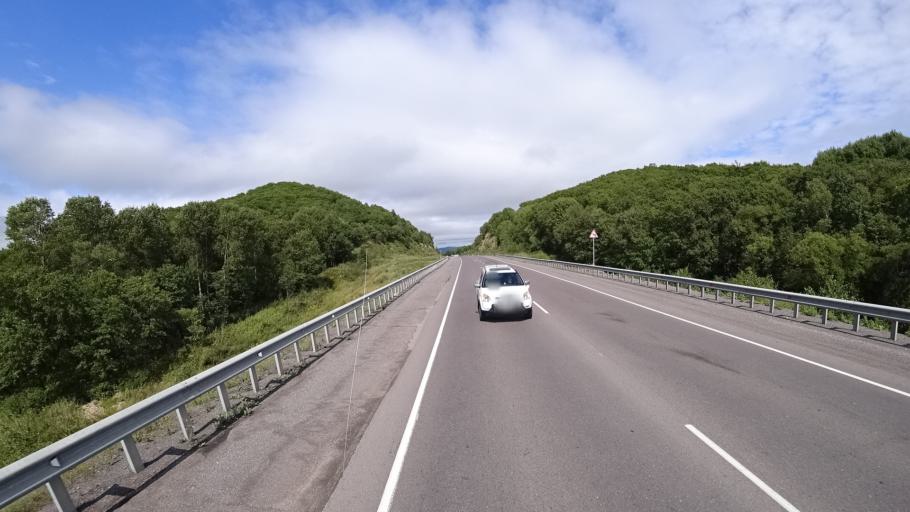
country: RU
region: Primorskiy
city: Lyalichi
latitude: 44.1262
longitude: 132.4243
